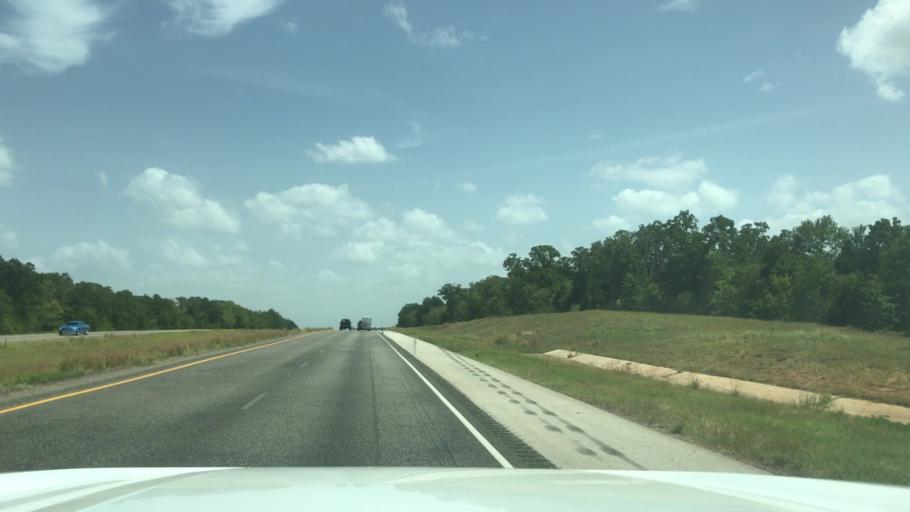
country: US
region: Texas
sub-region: Robertson County
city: Calvert
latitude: 30.9403
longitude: -96.6422
